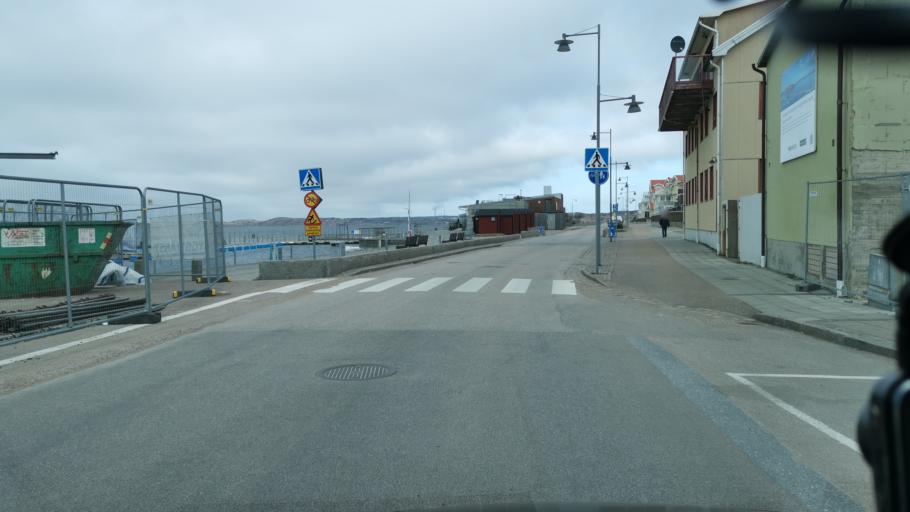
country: SE
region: Vaestra Goetaland
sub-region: Lysekils Kommun
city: Lysekil
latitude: 58.2767
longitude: 11.4251
